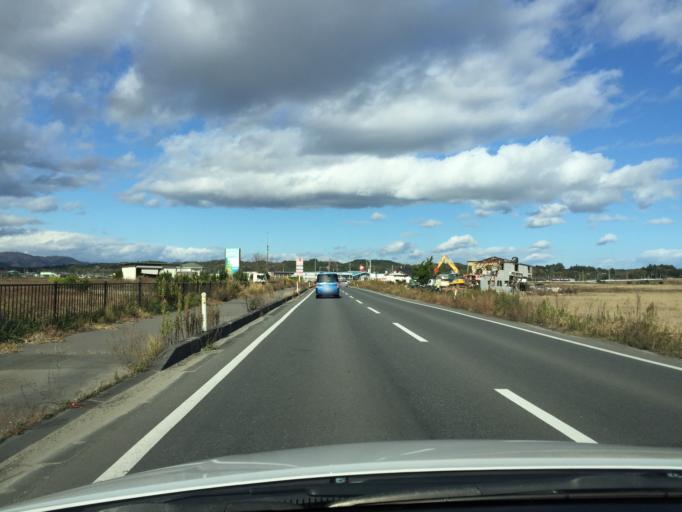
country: JP
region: Fukushima
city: Namie
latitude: 37.5574
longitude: 141.0037
